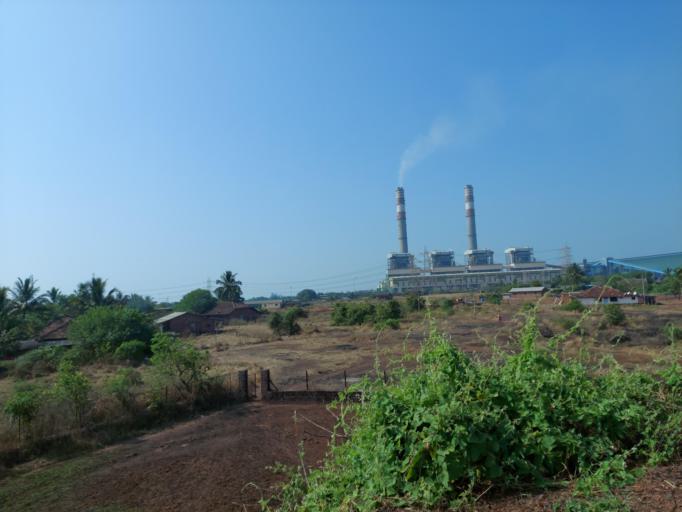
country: IN
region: Maharashtra
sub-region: Ratnagiri
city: Guhagar
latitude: 17.3001
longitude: 73.2211
